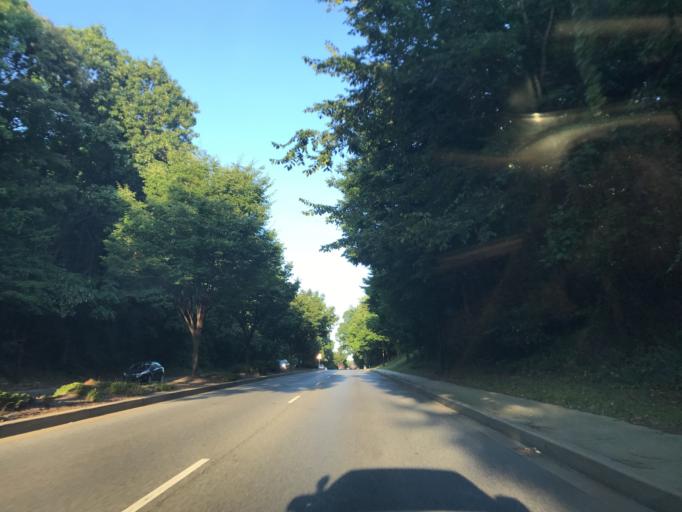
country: US
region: Maryland
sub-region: Anne Arundel County
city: Hillsmere Shores
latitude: 38.9516
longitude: -76.4981
